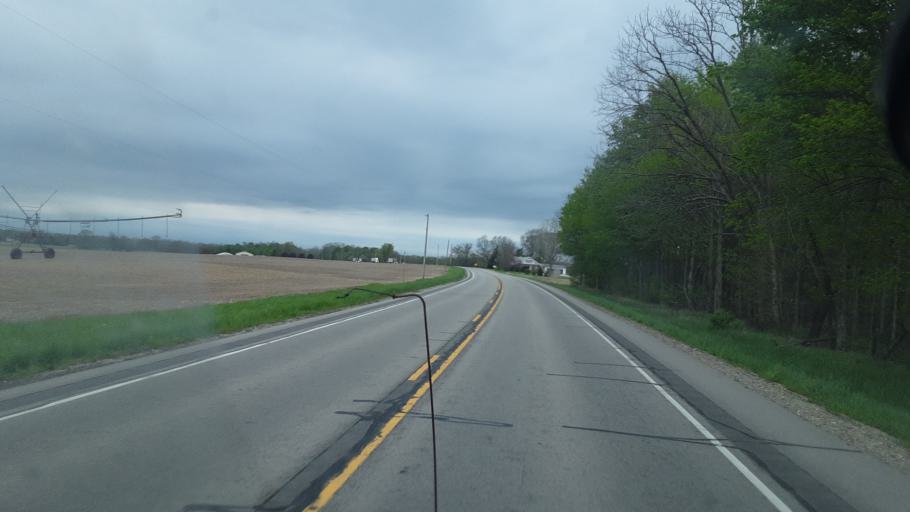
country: US
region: Indiana
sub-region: Kosciusko County
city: Syracuse
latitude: 41.4995
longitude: -85.7316
